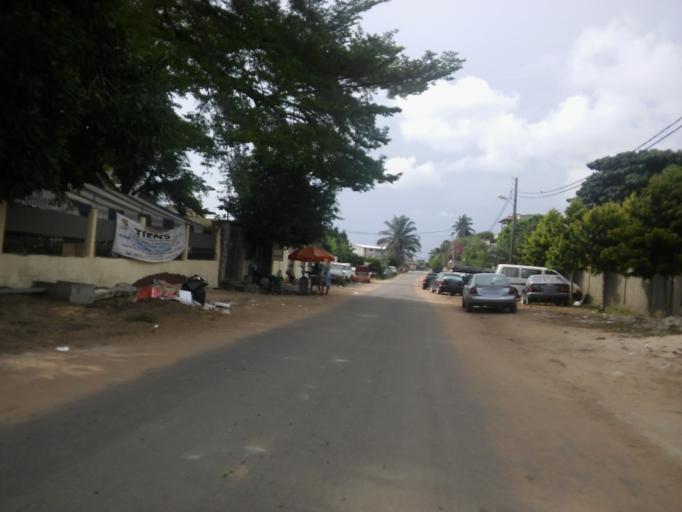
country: CI
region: Sud-Comoe
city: Grand-Bassam
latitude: 5.2068
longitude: -3.7322
